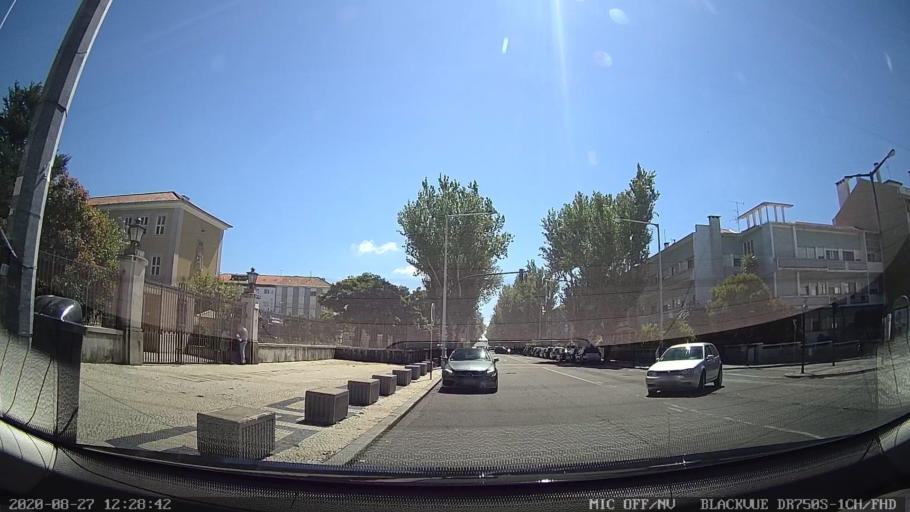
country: PT
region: Aveiro
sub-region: Aveiro
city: Aveiro
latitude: 40.6376
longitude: -8.6487
